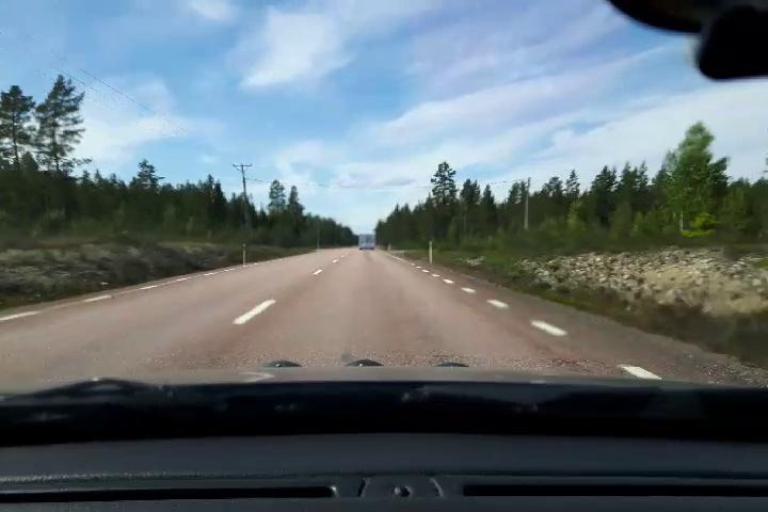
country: SE
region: Gaevleborg
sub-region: Soderhamns Kommun
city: Soderhamn
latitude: 61.1359
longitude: 16.9156
